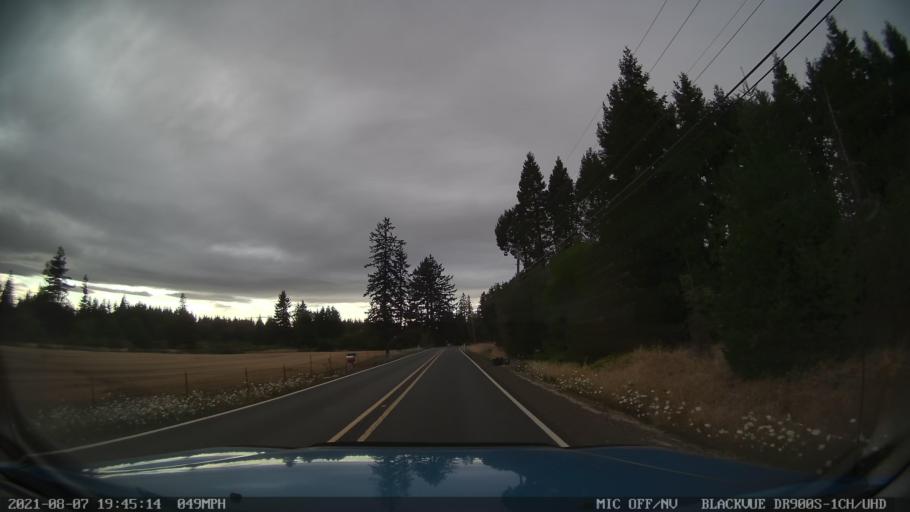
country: US
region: Oregon
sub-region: Marion County
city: Silverton
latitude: 44.9463
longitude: -122.6934
